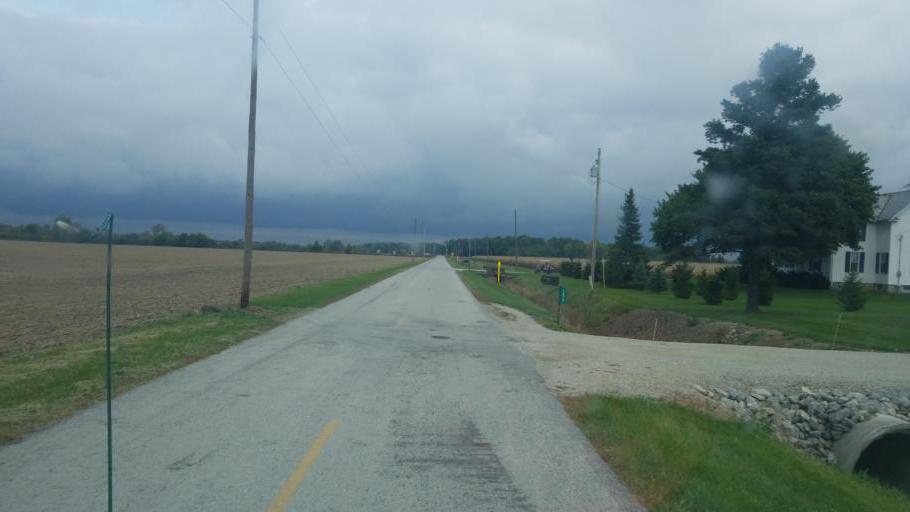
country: US
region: Ohio
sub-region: Wood County
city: North Baltimore
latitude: 41.1683
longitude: -83.5928
